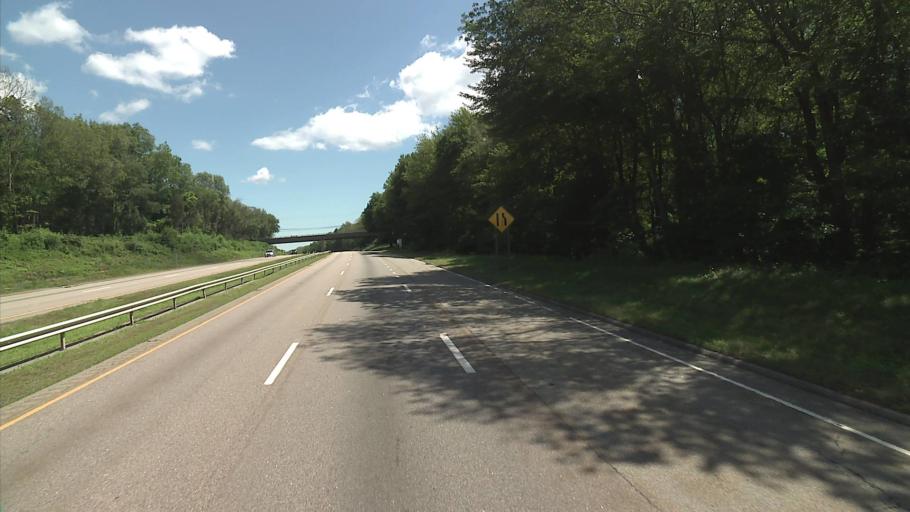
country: US
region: Connecticut
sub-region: New London County
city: Oxoboxo River
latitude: 41.4013
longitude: -72.1536
